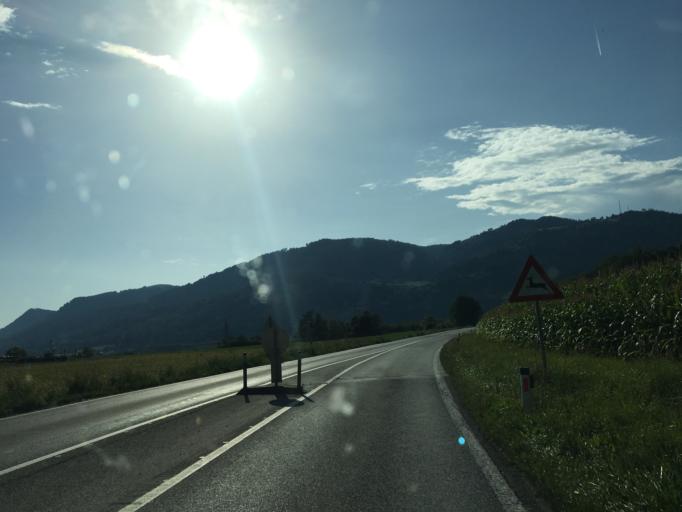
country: AT
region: Carinthia
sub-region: Politischer Bezirk Sankt Veit an der Glan
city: Bruckl
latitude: 46.7243
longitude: 14.5421
